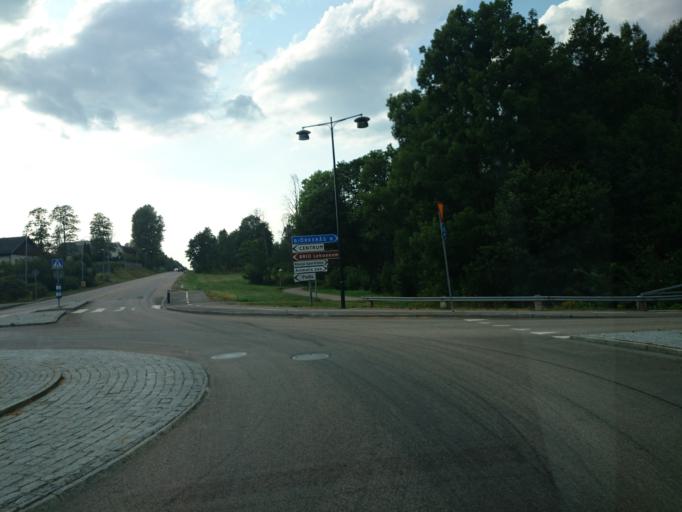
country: SE
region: Skane
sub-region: Osby Kommun
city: Osby
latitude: 56.3850
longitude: 13.9969
